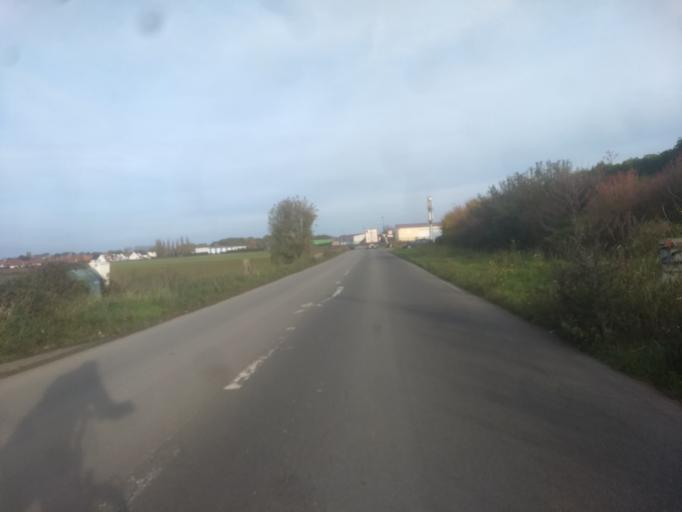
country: FR
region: Nord-Pas-de-Calais
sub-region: Departement du Pas-de-Calais
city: Agny
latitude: 50.2538
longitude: 2.7742
